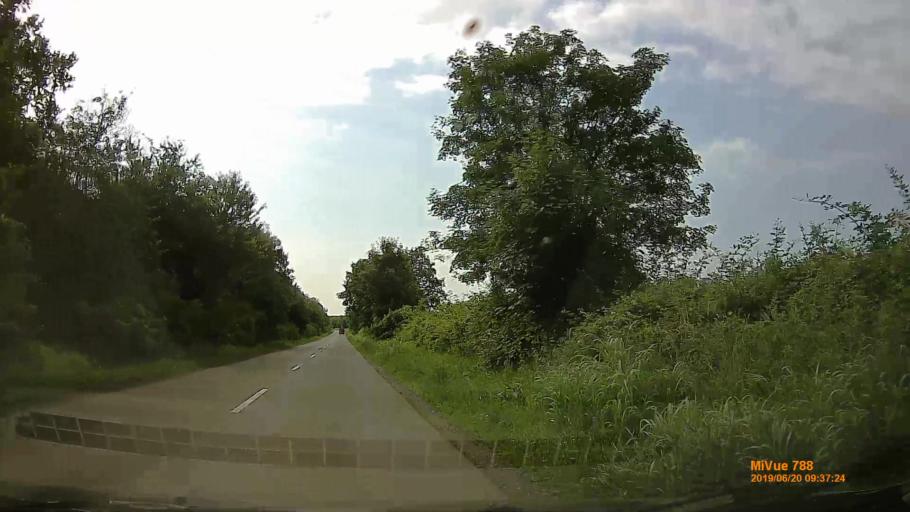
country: HU
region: Baranya
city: Pecsvarad
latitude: 46.1634
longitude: 18.4635
